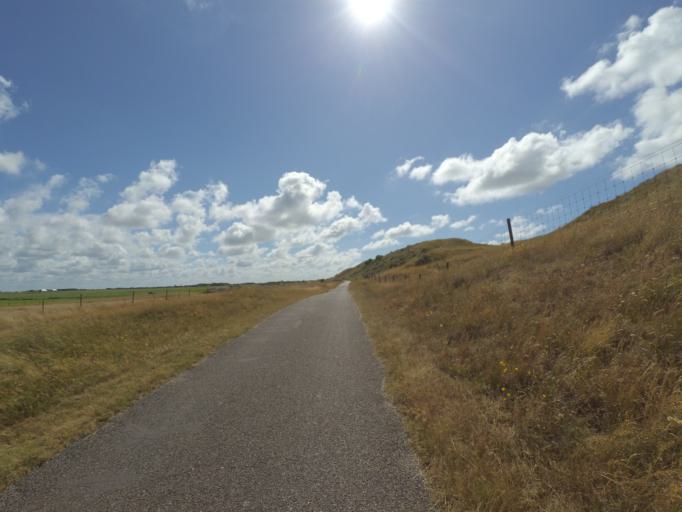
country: NL
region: North Holland
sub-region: Gemeente Texel
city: Den Burg
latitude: 53.1413
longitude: 4.8289
